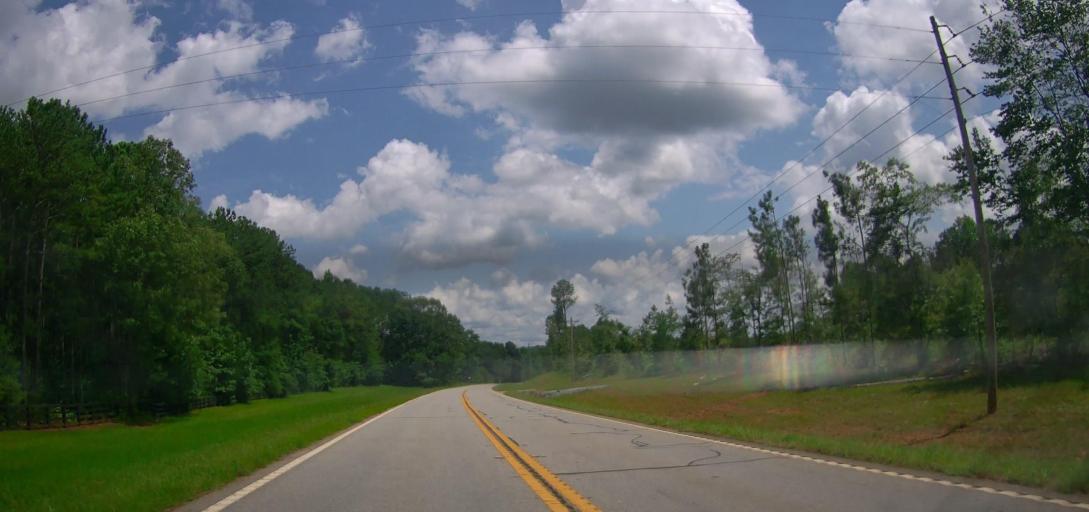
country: US
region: Georgia
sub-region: Heard County
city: Franklin
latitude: 33.3342
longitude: -85.1625
